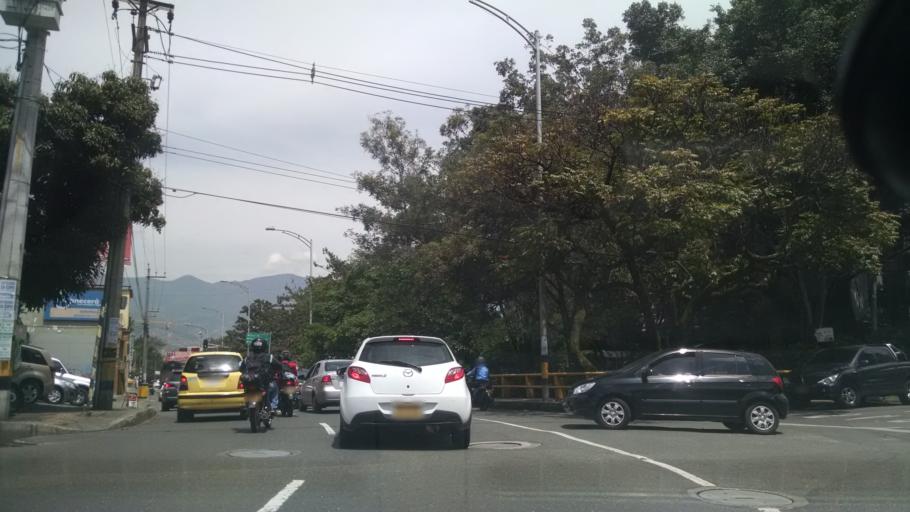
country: CO
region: Antioquia
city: Itagui
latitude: 6.2117
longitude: -75.5707
